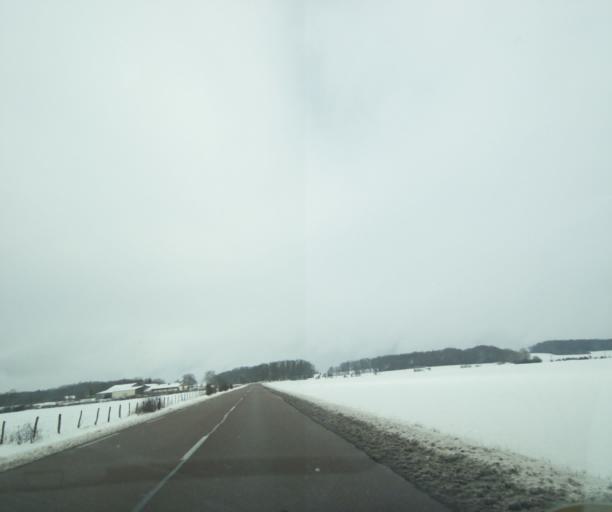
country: FR
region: Champagne-Ardenne
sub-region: Departement de la Haute-Marne
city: Montier-en-Der
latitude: 48.4452
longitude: 4.7347
